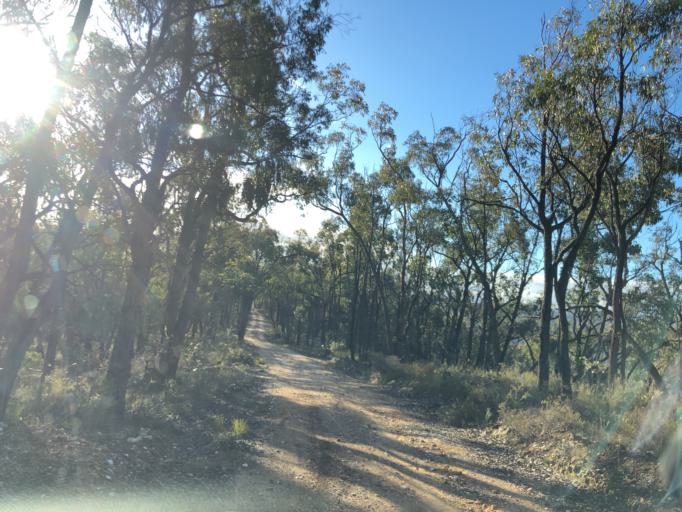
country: AU
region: Victoria
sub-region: Mount Alexander
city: Castlemaine
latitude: -37.2321
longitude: 144.2694
